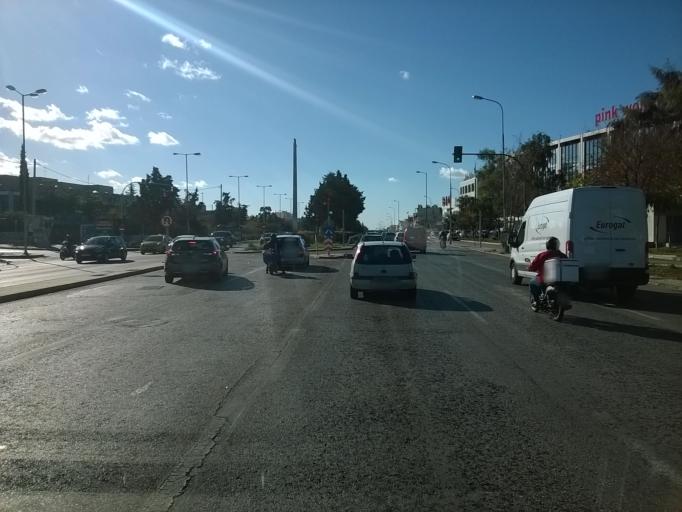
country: GR
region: Attica
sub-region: Nomarchia Athinas
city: Agios Dimitrios
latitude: 37.9241
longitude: 23.7443
